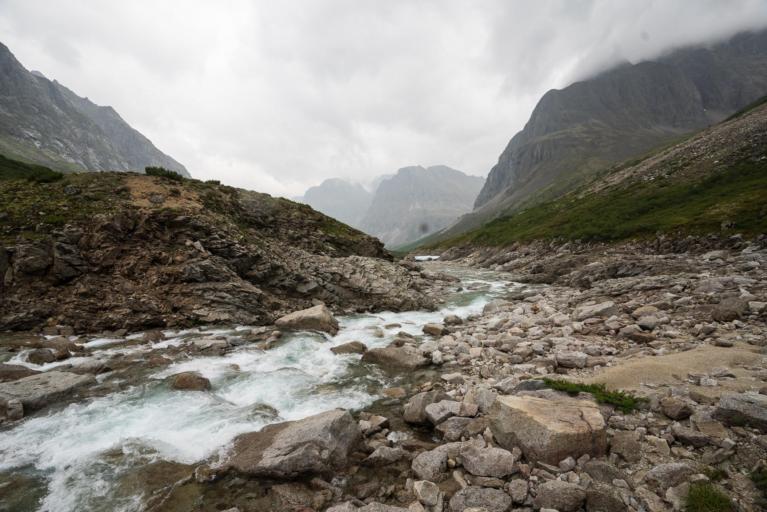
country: RU
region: Transbaikal Territory
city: Chara
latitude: 56.9402
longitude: 117.6171
